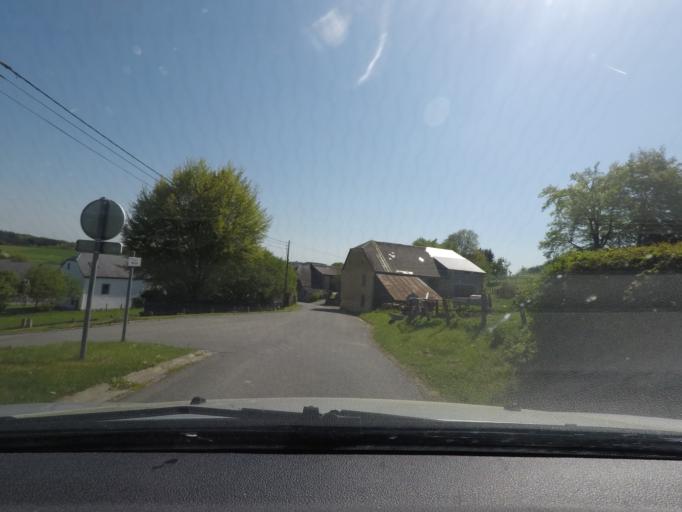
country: BE
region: Wallonia
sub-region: Province du Luxembourg
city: Leglise
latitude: 49.7853
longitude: 5.4830
